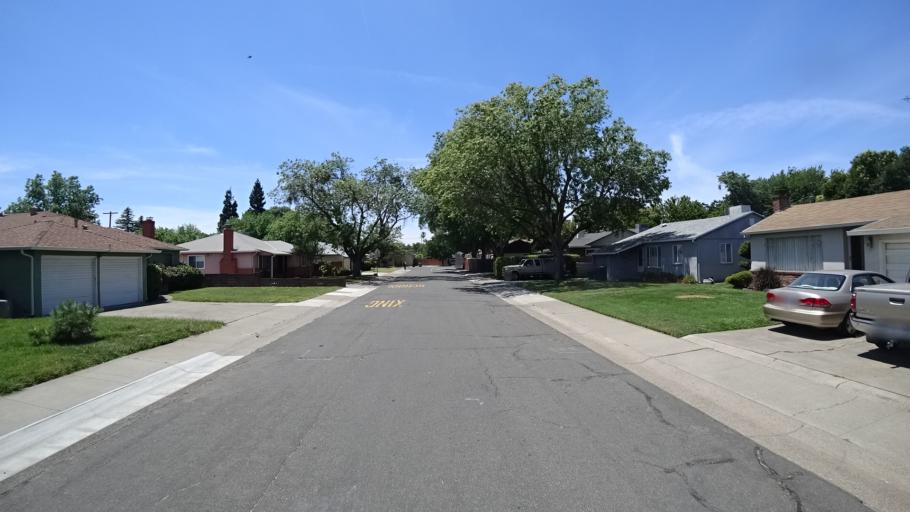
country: US
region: California
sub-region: Sacramento County
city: Florin
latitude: 38.5332
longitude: -121.4201
